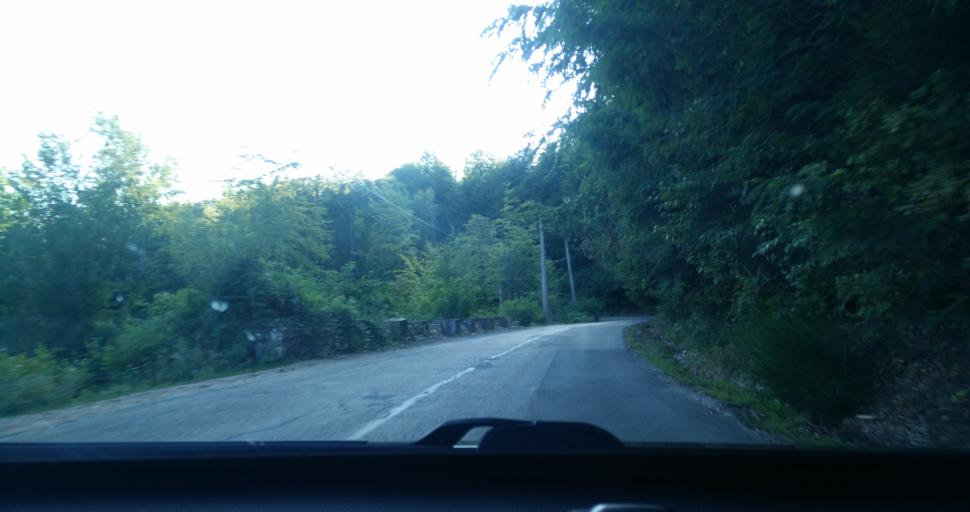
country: RO
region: Bihor
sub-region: Oras Nucet
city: Nucet
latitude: 46.5035
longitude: 22.6157
